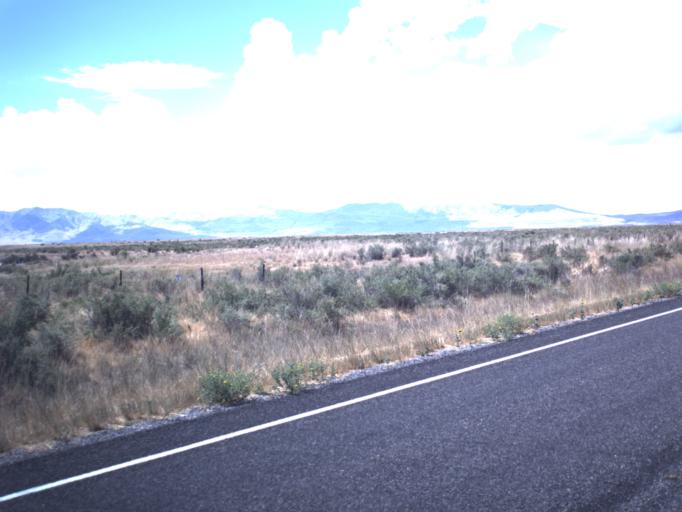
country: US
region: Utah
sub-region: Box Elder County
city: Tremonton
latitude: 41.5908
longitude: -112.2751
